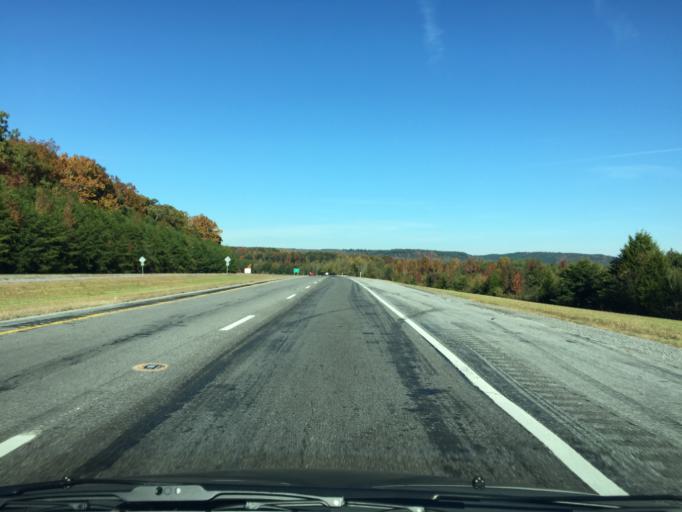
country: US
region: Tennessee
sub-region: Hamilton County
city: Sale Creek
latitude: 35.3408
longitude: -85.1683
